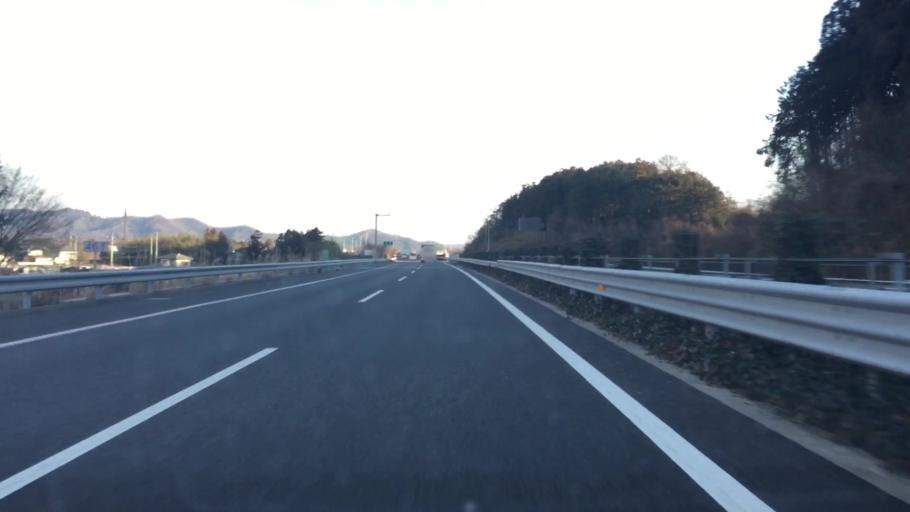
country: JP
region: Tochigi
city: Tanuma
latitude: 36.3704
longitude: 139.5423
